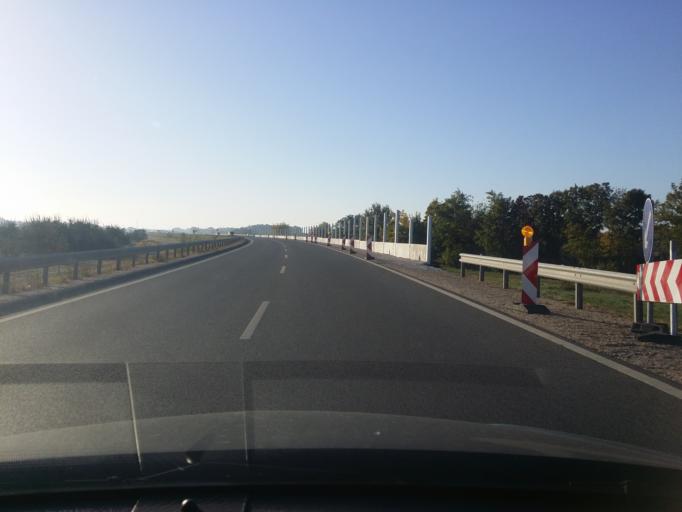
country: HU
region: Bacs-Kiskun
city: Kecskemet
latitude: 46.9281
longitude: 19.7158
